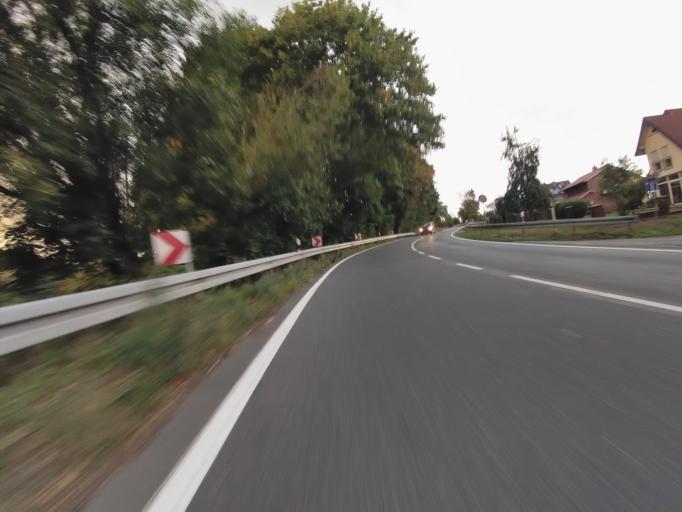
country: DE
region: North Rhine-Westphalia
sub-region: Regierungsbezirk Munster
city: Tecklenburg
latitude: 52.2753
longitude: 7.8268
